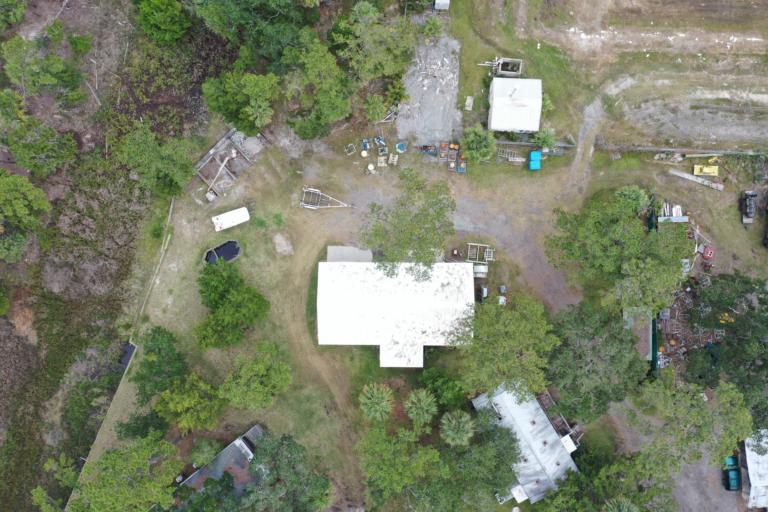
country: US
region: Georgia
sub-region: Chatham County
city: Isle of Hope
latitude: 31.9887
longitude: -81.0219
